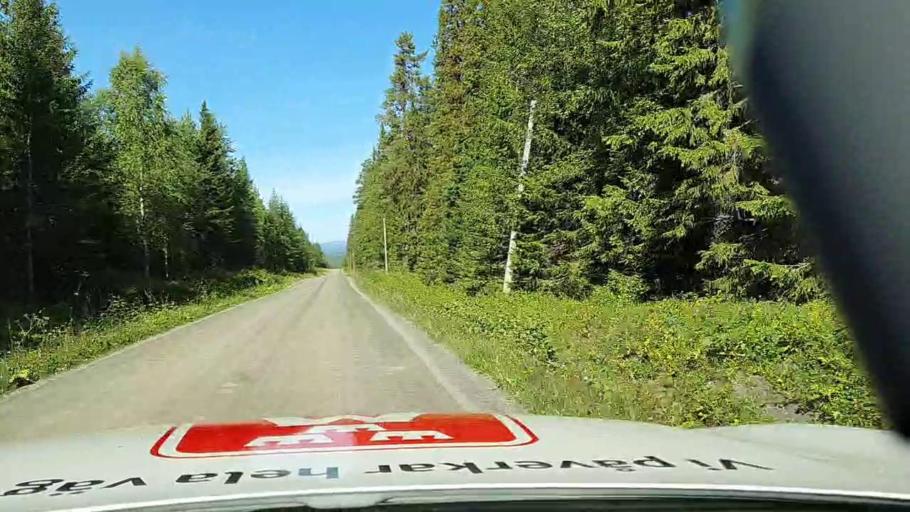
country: SE
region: Jaemtland
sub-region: Krokoms Kommun
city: Krokom
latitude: 63.7001
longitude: 14.6103
